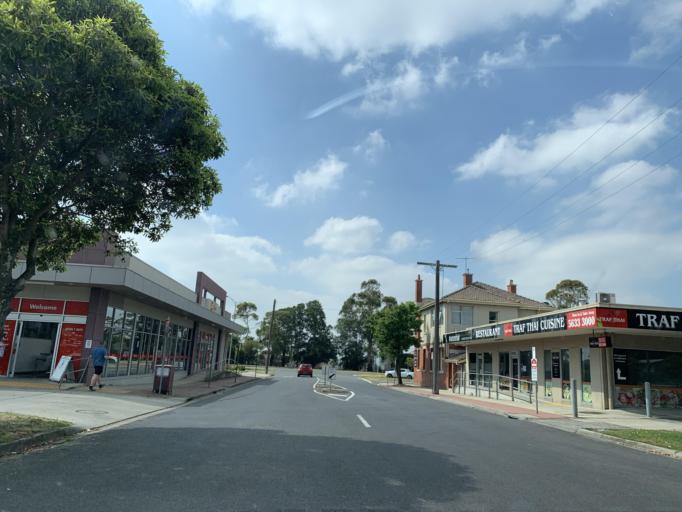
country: AU
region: Victoria
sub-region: Latrobe
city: Moe
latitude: -38.2088
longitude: 146.1537
